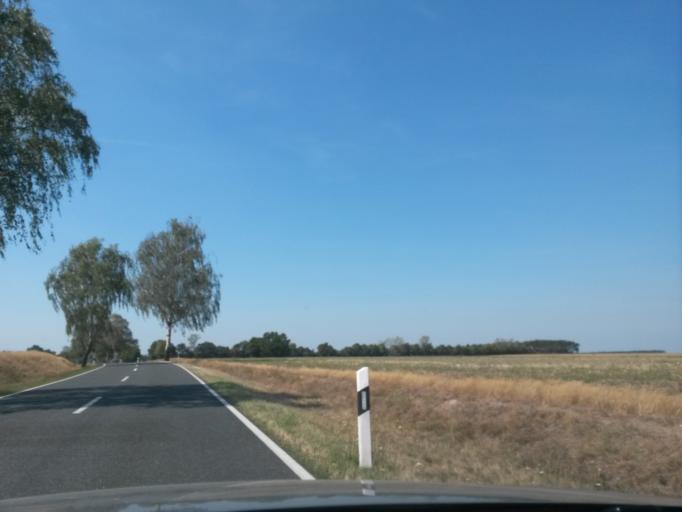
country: DE
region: Brandenburg
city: Gorzke
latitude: 52.1729
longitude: 12.3988
